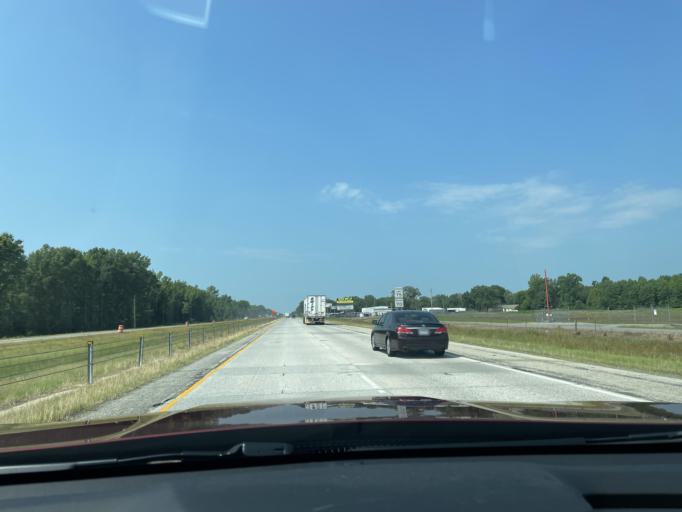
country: US
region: Arkansas
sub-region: White County
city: Searcy
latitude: 35.1970
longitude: -91.7404
